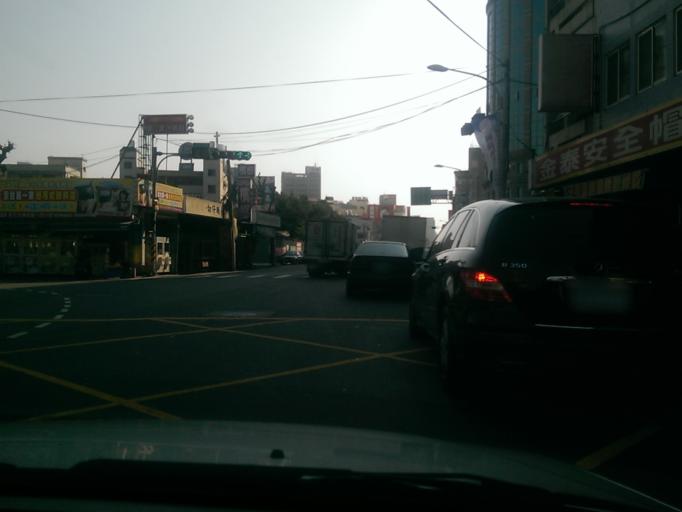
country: TW
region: Taiwan
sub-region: Changhua
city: Chang-hua
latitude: 24.0753
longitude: 120.5440
